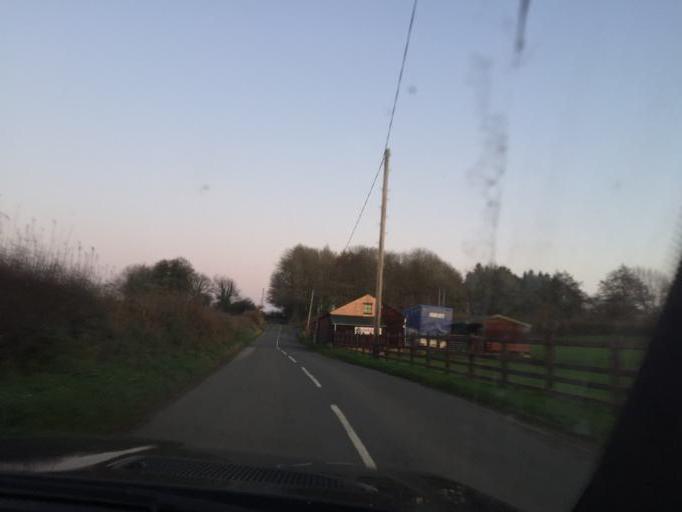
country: GB
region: England
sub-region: Northamptonshire
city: Brackley
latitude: 52.0960
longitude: -1.1129
